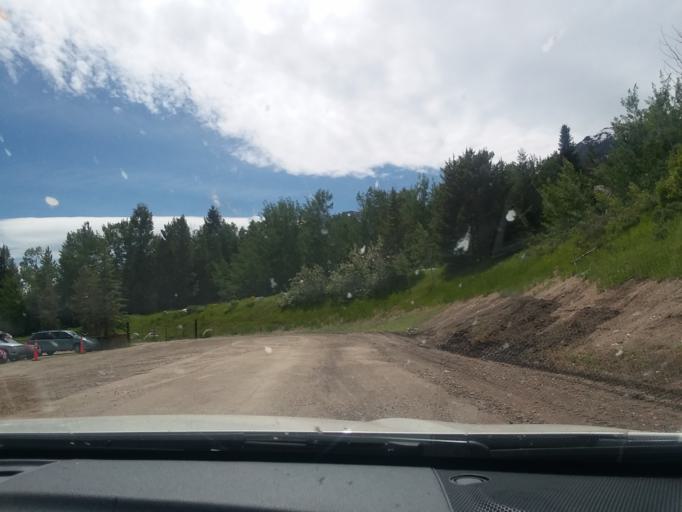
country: US
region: Wyoming
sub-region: Teton County
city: Moose Wilson Road
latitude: 43.5874
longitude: -110.8309
